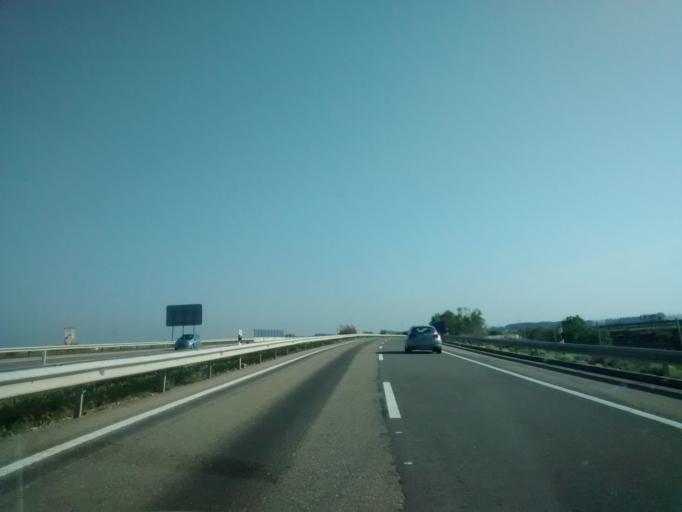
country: ES
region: Aragon
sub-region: Provincia de Zaragoza
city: Zuera
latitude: 41.8969
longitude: -0.7658
